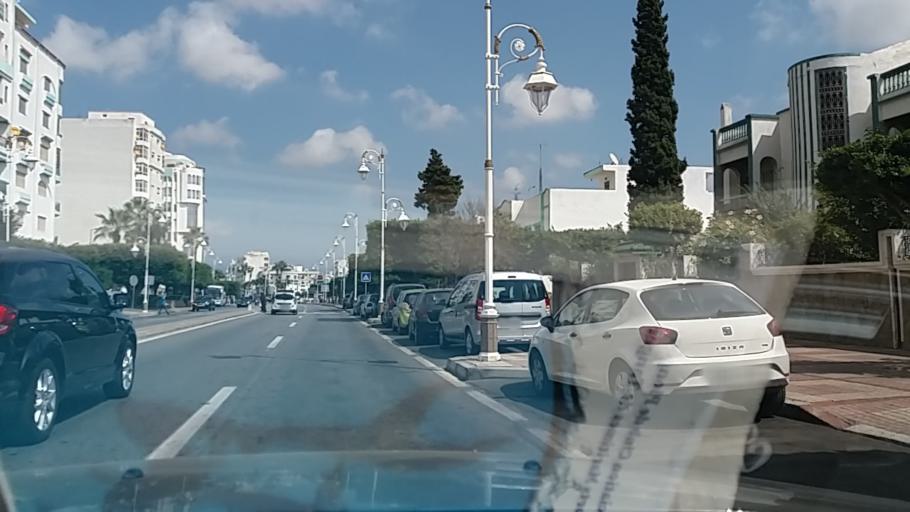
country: MA
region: Tanger-Tetouan
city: Tetouan
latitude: 35.5842
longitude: -5.3495
